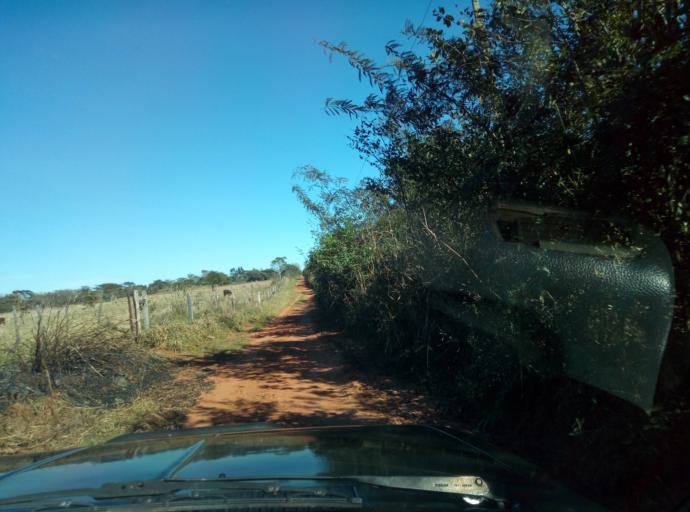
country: PY
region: Caaguazu
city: Doctor Cecilio Baez
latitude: -25.1790
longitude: -56.2365
